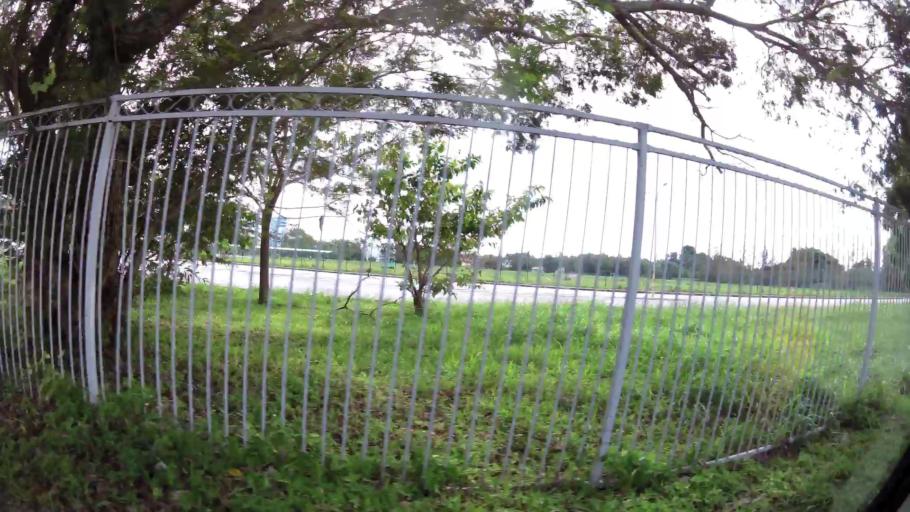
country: BN
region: Brunei and Muara
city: Bandar Seri Begawan
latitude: 4.9479
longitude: 114.9511
